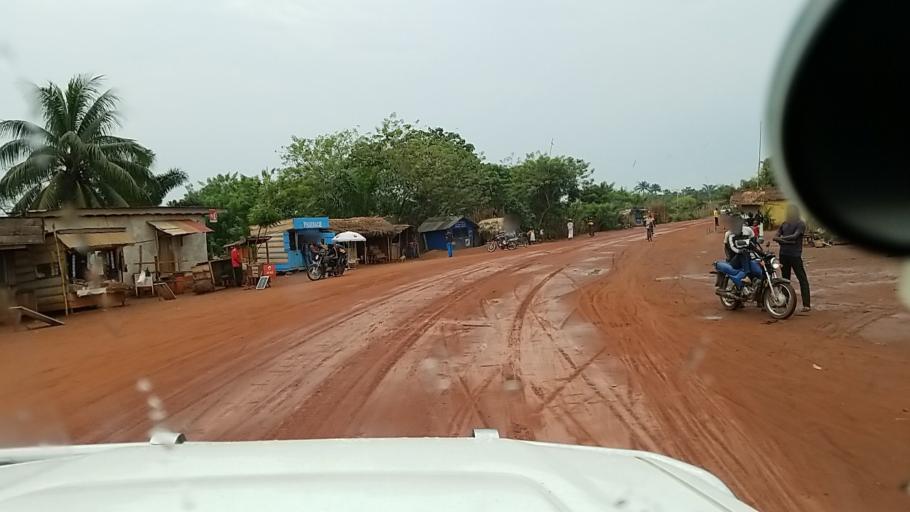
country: CD
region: Equateur
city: Gemena
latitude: 3.2321
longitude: 19.7816
